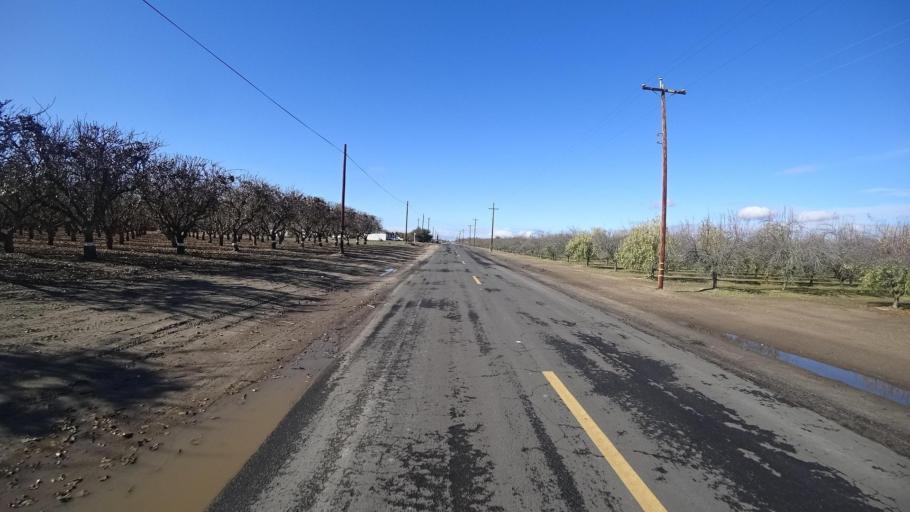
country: US
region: California
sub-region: Kern County
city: Rosedale
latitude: 35.3689
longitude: -119.2085
